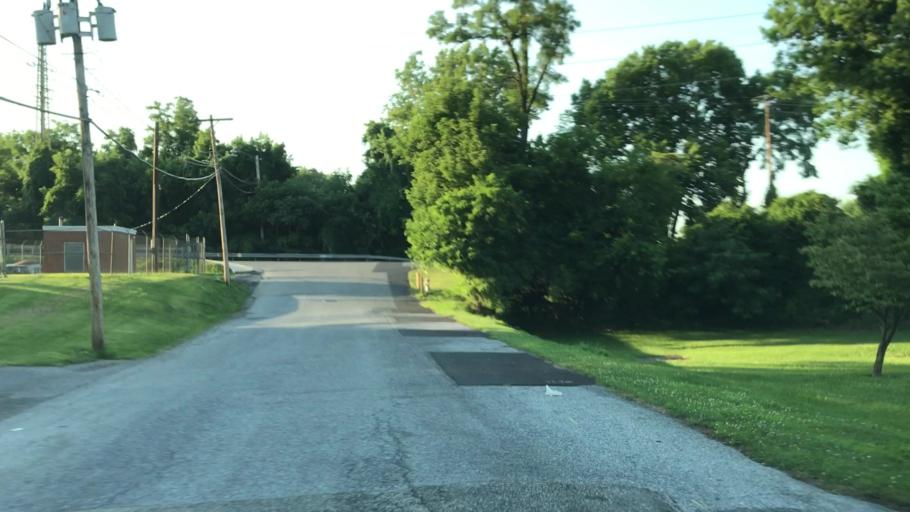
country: US
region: Pennsylvania
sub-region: Dauphin County
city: Middletown
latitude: 40.1883
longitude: -76.7318
